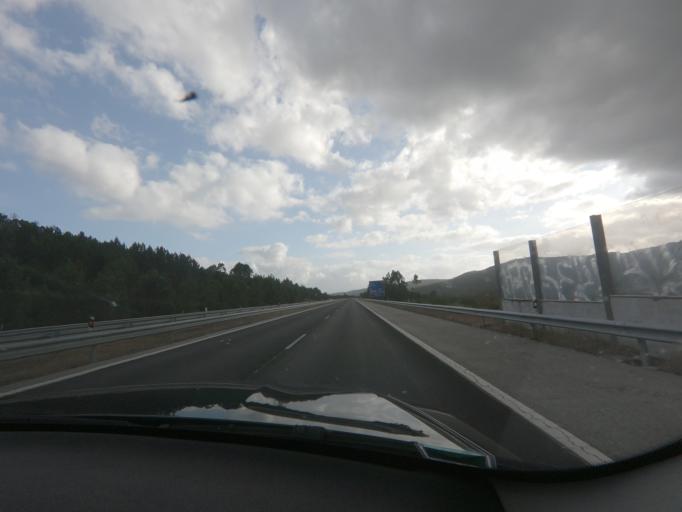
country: PT
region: Viseu
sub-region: Castro Daire
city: Castro Daire
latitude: 40.8725
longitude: -7.9240
